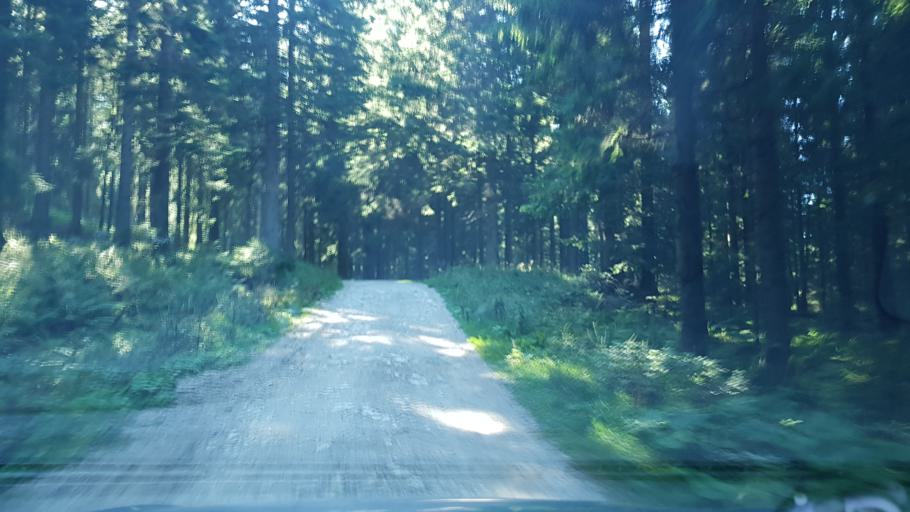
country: SI
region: Ravne na Koroskem
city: Kotlje
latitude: 46.4850
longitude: 14.9777
